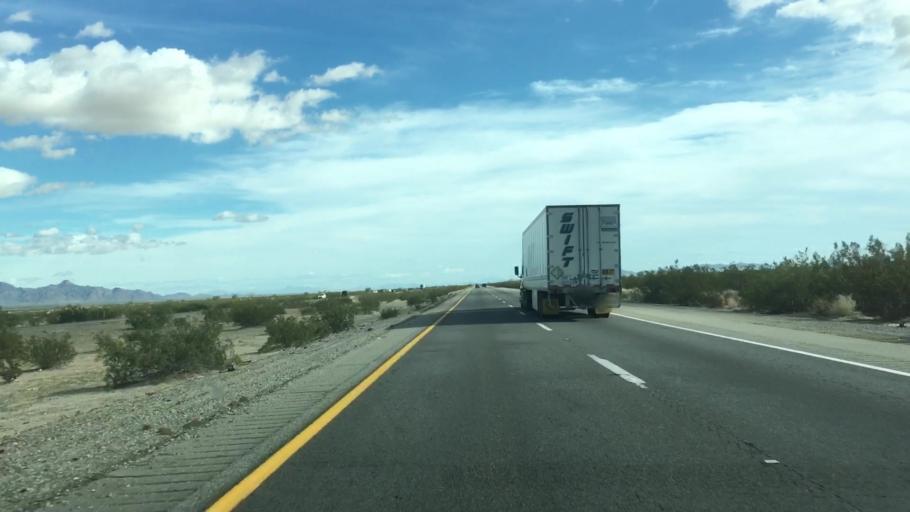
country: US
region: California
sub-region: Riverside County
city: Mesa Verde
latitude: 33.6276
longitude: -115.0628
